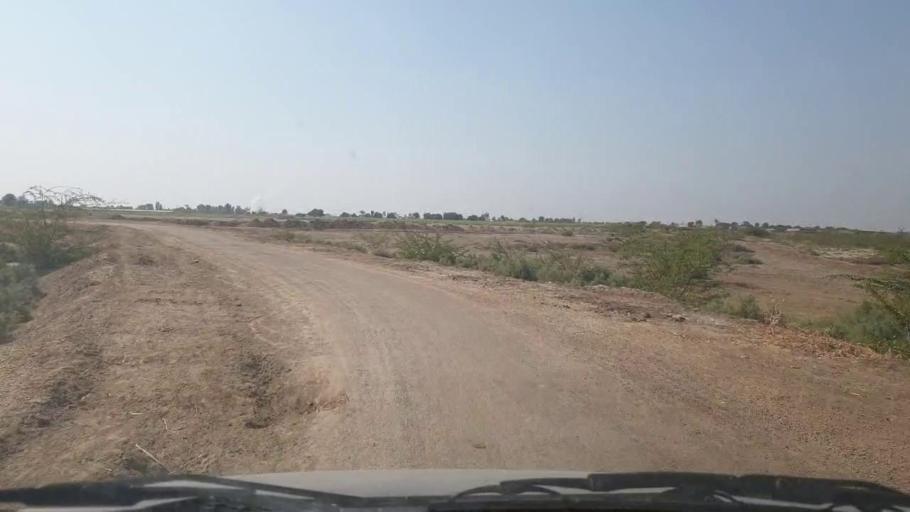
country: PK
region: Sindh
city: Samaro
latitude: 25.2568
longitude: 69.3245
